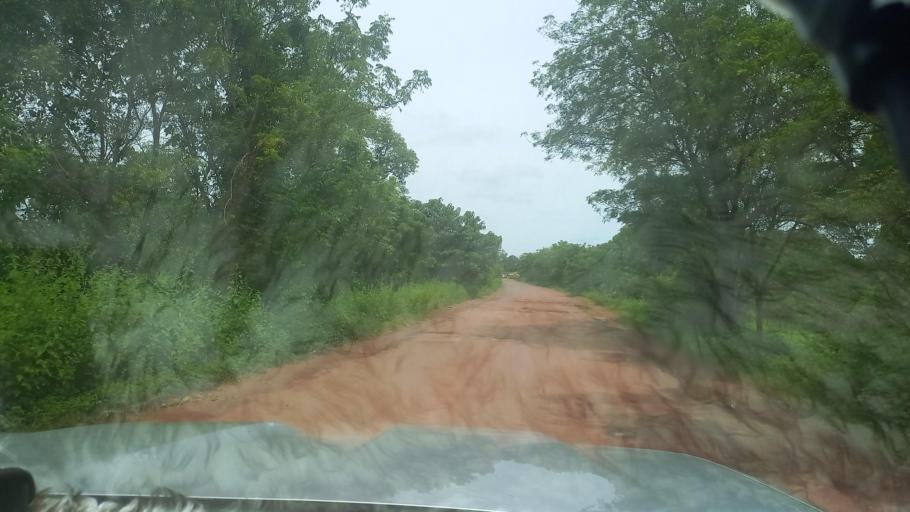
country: SN
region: Kolda
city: Marsassoum
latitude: 12.9120
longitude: -16.0107
